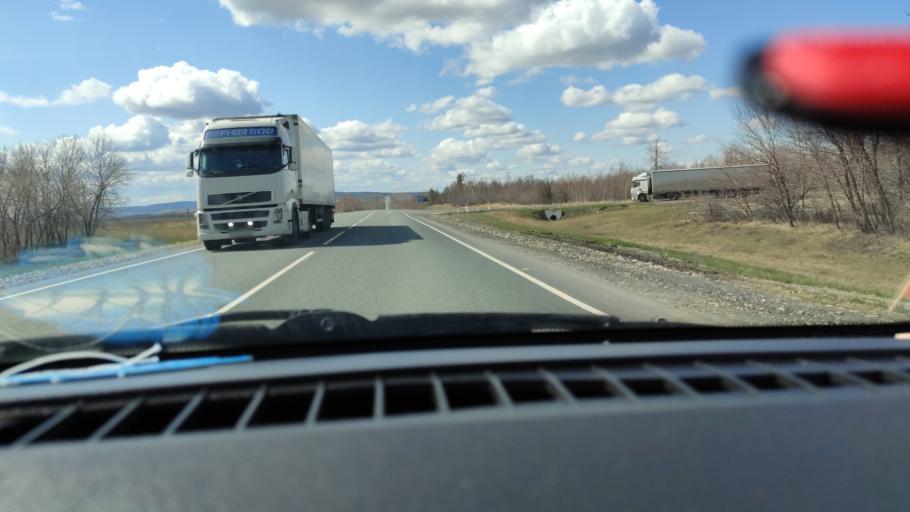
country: RU
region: Saratov
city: Khvalynsk
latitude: 52.5842
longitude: 48.1211
